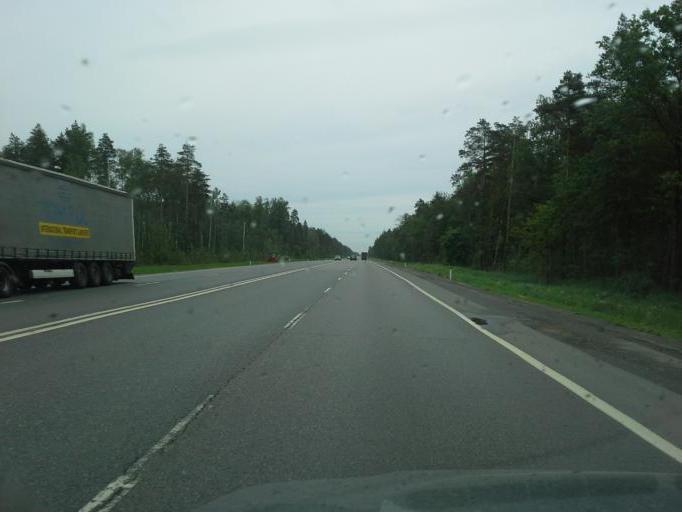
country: RU
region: Vladimir
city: Pokrov
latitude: 55.9072
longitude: 39.1061
